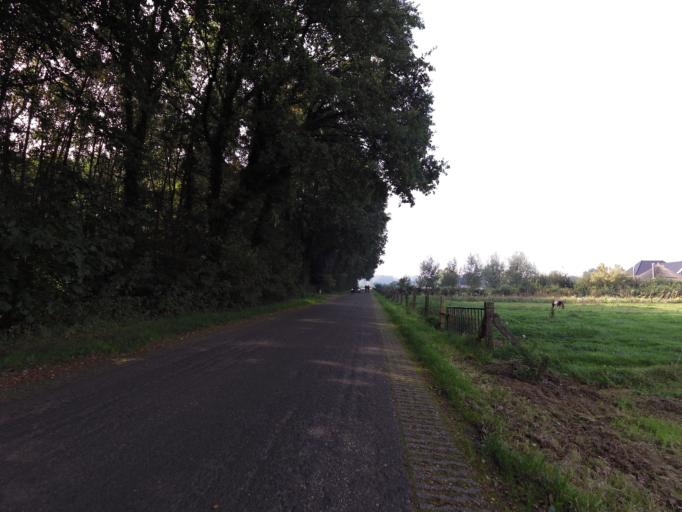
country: NL
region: Gelderland
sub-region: Gemeente Doetinchem
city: Doetinchem
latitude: 51.9516
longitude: 6.2082
